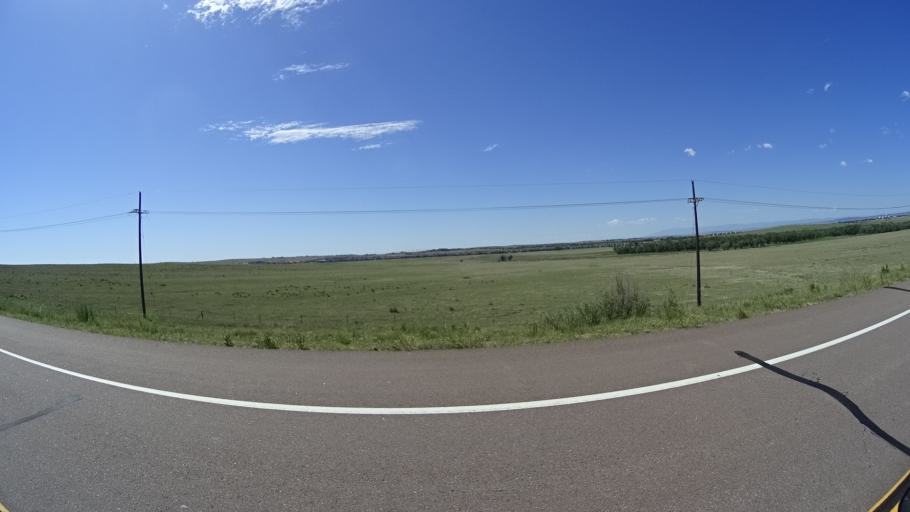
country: US
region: Colorado
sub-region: El Paso County
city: Security-Widefield
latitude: 38.7628
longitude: -104.6403
